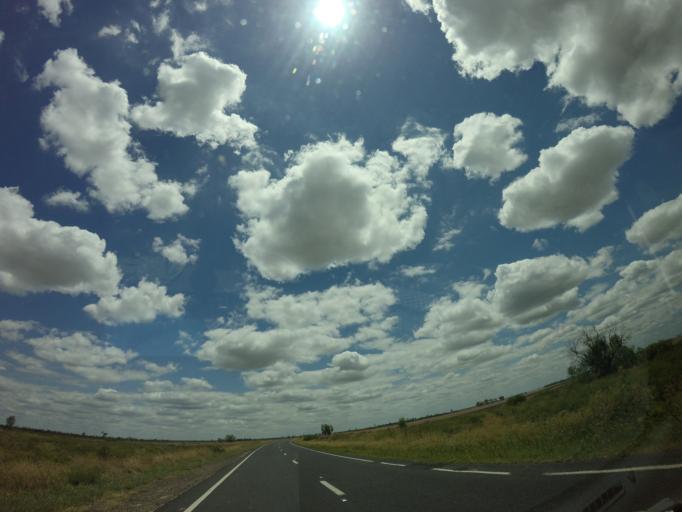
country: AU
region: New South Wales
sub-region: Moree Plains
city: Boggabilla
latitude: -28.7057
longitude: 150.2802
